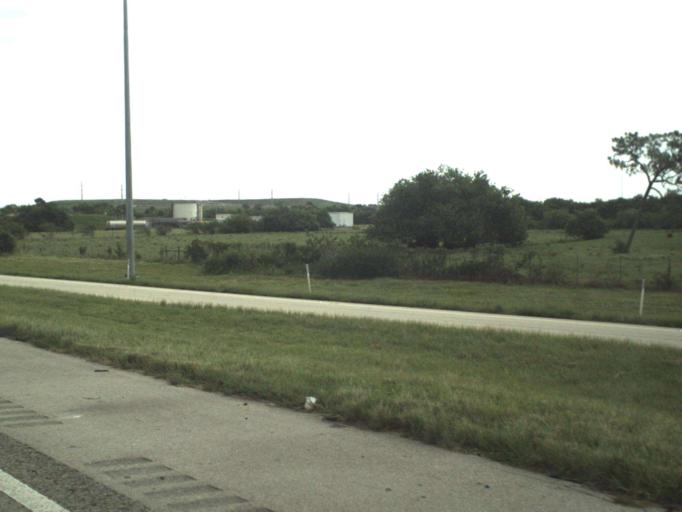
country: US
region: Florida
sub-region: Saint Lucie County
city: Fort Pierce South
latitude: 27.3780
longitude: -80.4073
